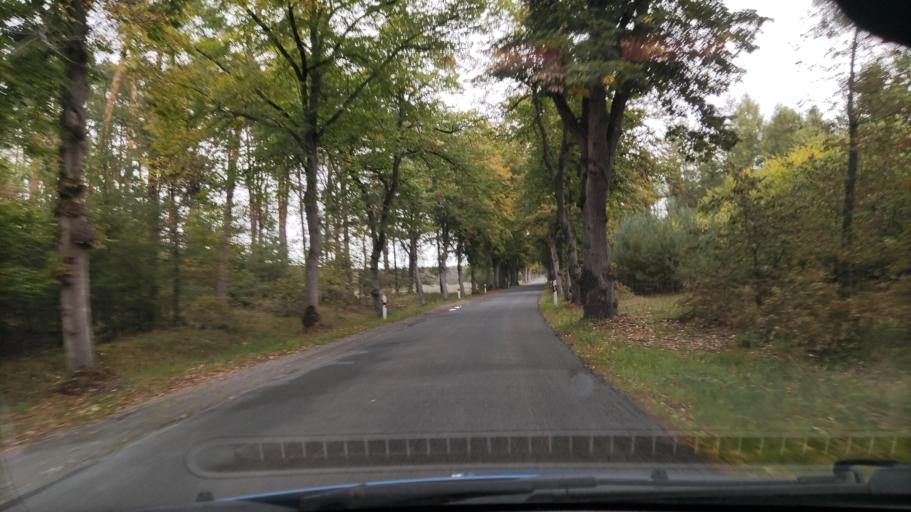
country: DE
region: Saxony-Anhalt
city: Luftkurort Arendsee
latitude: 52.9433
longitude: 11.5321
